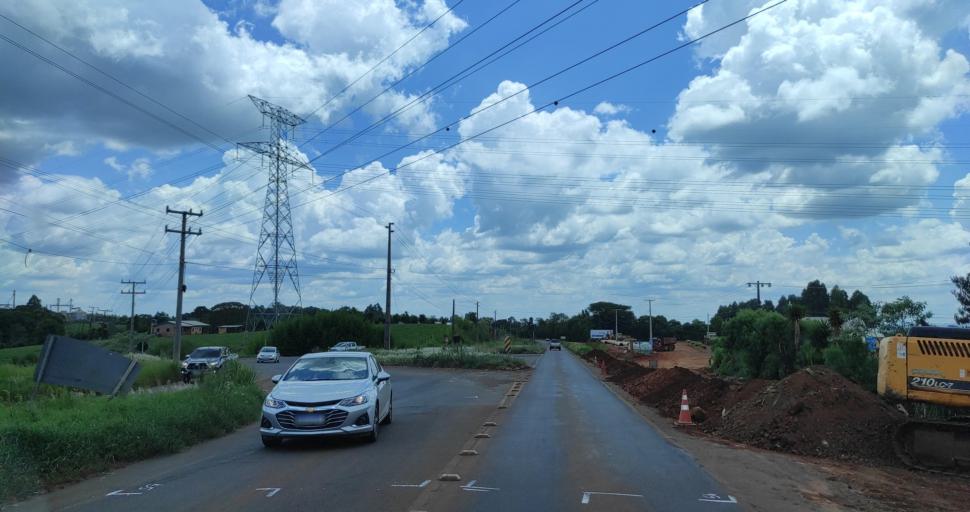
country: BR
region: Santa Catarina
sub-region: Xanxere
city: Xanxere
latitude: -26.8443
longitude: -52.4076
